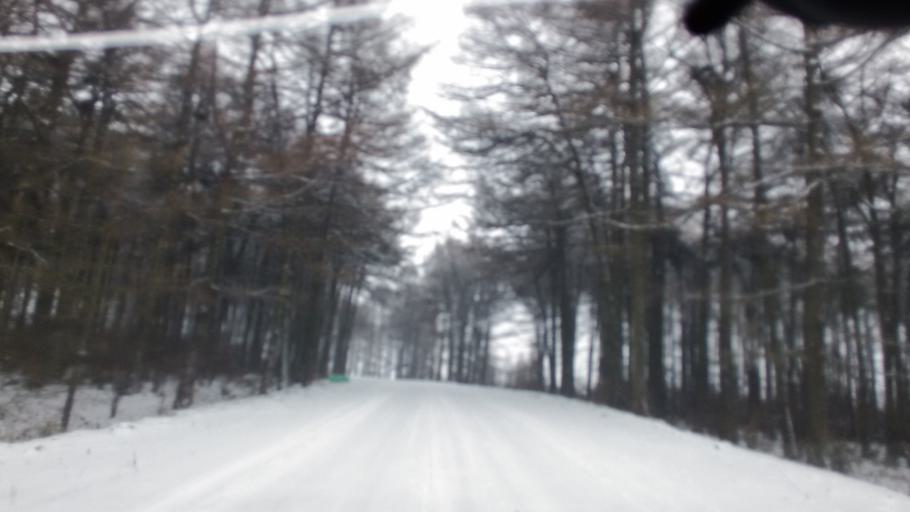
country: RU
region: Tula
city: Volovo
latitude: 53.6853
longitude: 37.9284
